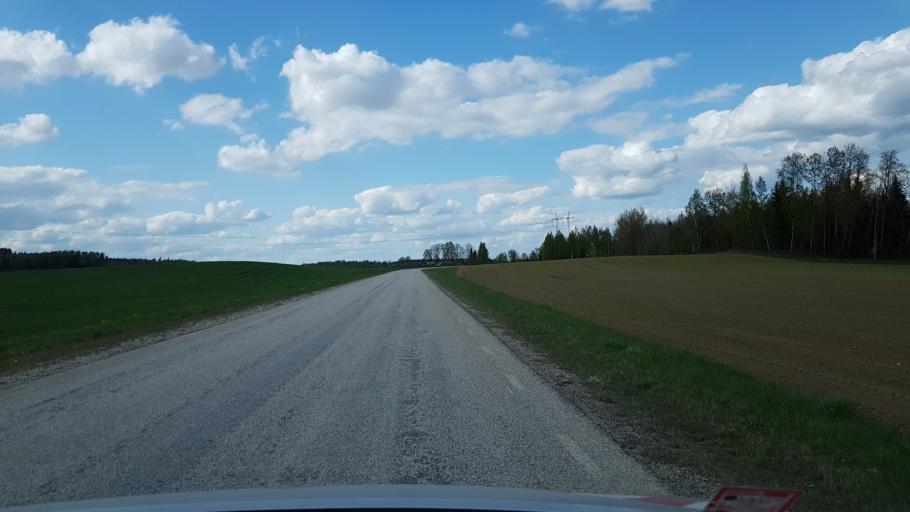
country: EE
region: Tartu
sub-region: UElenurme vald
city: Ulenurme
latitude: 58.2715
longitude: 26.9082
